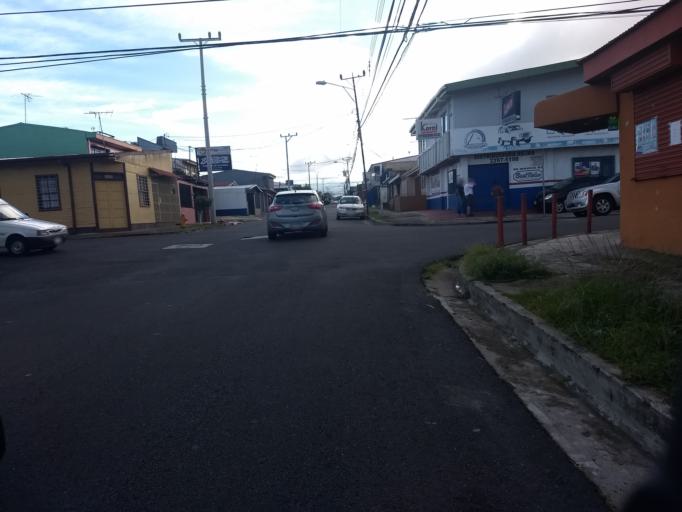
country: CR
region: San Jose
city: San Juan
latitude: 9.9589
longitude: -84.0813
